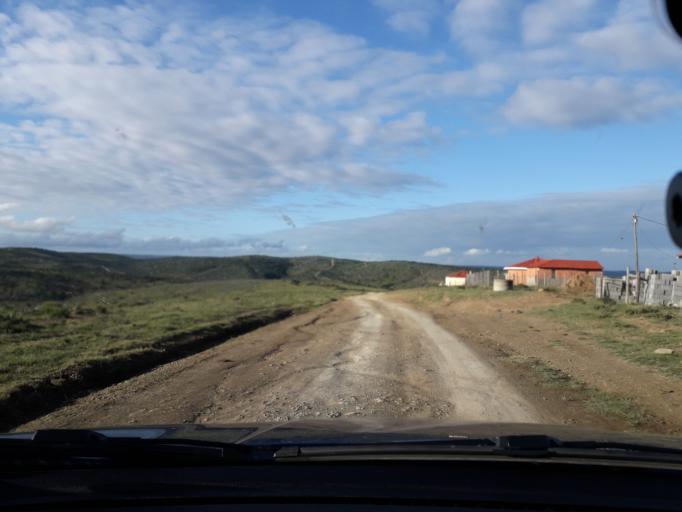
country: ZA
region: Eastern Cape
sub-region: Buffalo City Metropolitan Municipality
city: Bhisho
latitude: -33.1291
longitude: 27.4393
